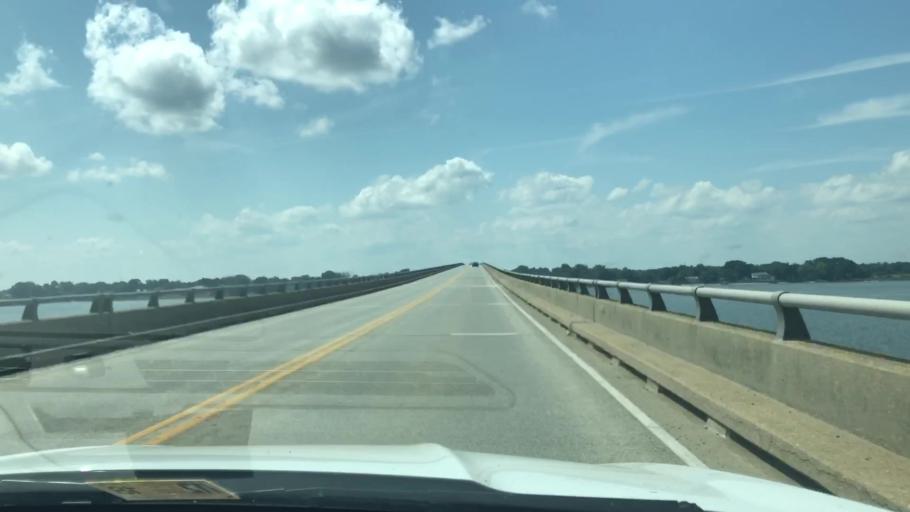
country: US
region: Virginia
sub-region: Essex County
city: Tappahannock
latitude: 37.9366
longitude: -76.8472
